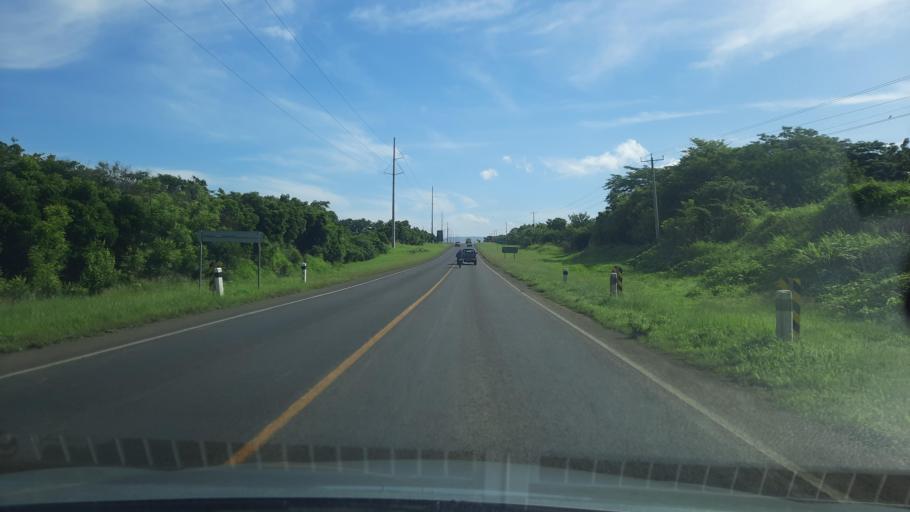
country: NI
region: Managua
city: Tipitapa
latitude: 12.3641
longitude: -86.0477
